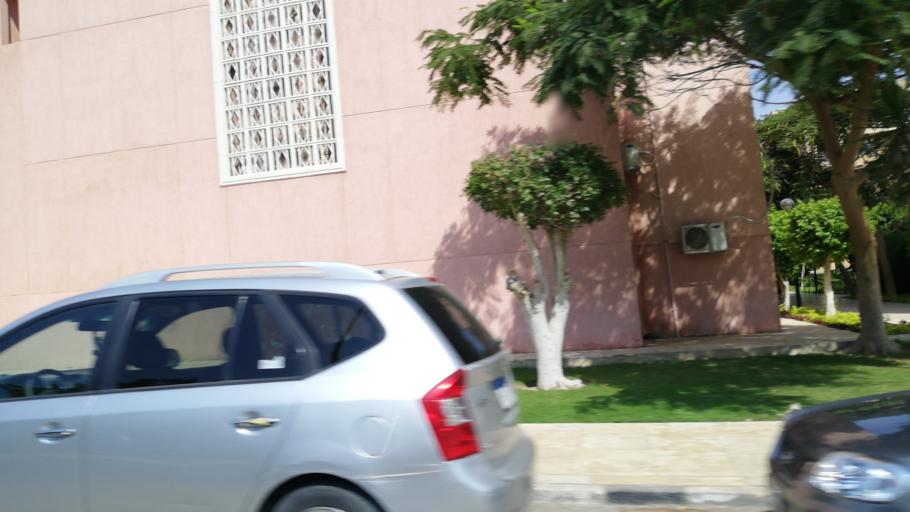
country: EG
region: Muhafazat al Qalyubiyah
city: Al Khankah
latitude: 30.0612
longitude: 31.4878
